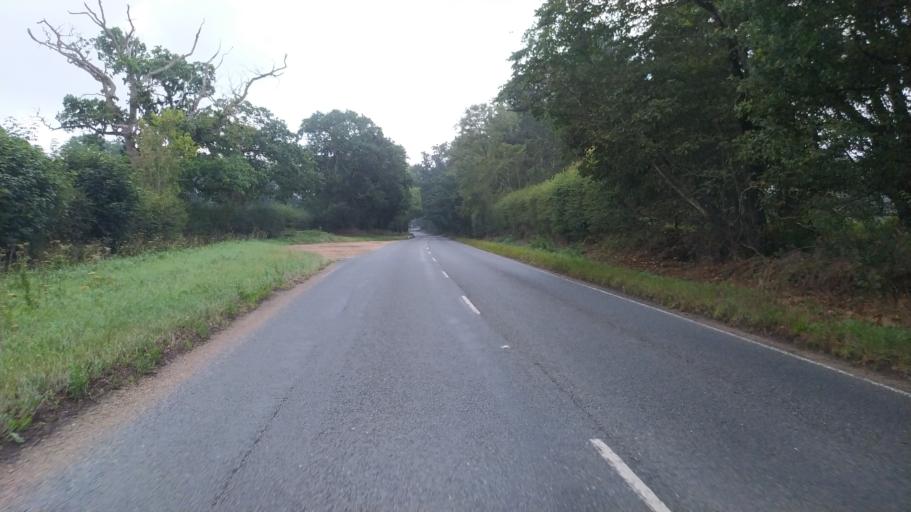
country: GB
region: England
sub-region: Hampshire
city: New Milton
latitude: 50.7680
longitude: -1.6974
